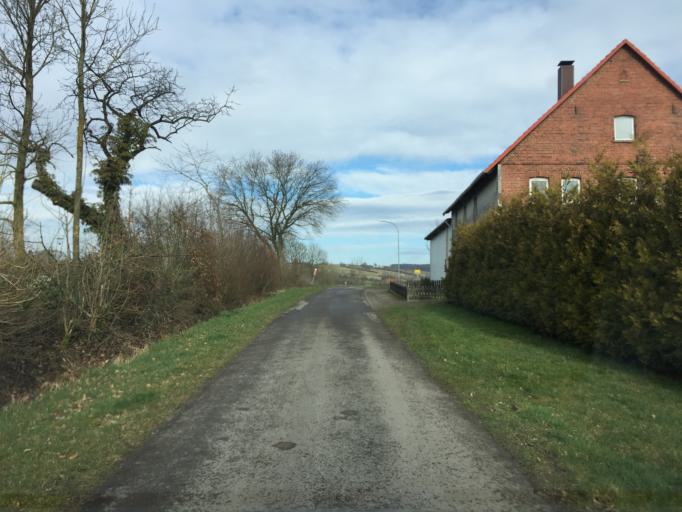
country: DE
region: Lower Saxony
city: Aerzen
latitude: 52.0964
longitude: 9.1628
